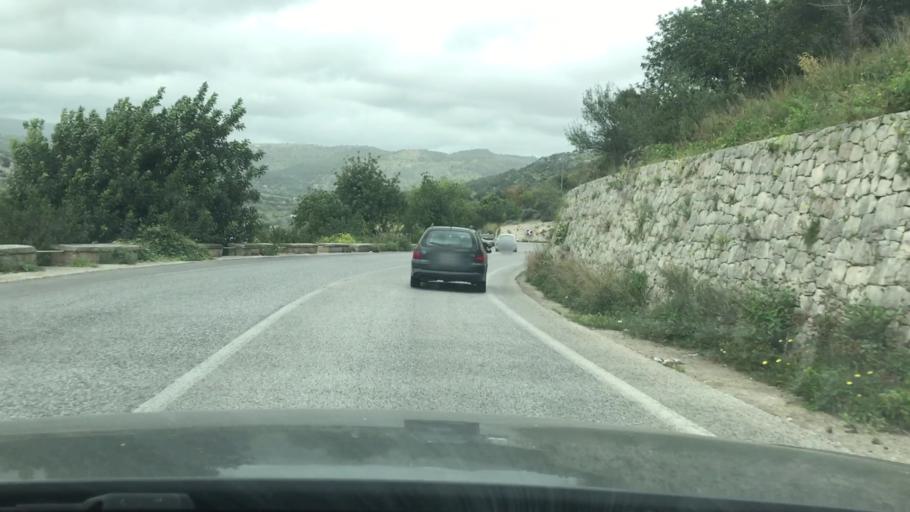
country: IT
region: Sicily
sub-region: Ragusa
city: Scicli
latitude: 36.7971
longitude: 14.7098
